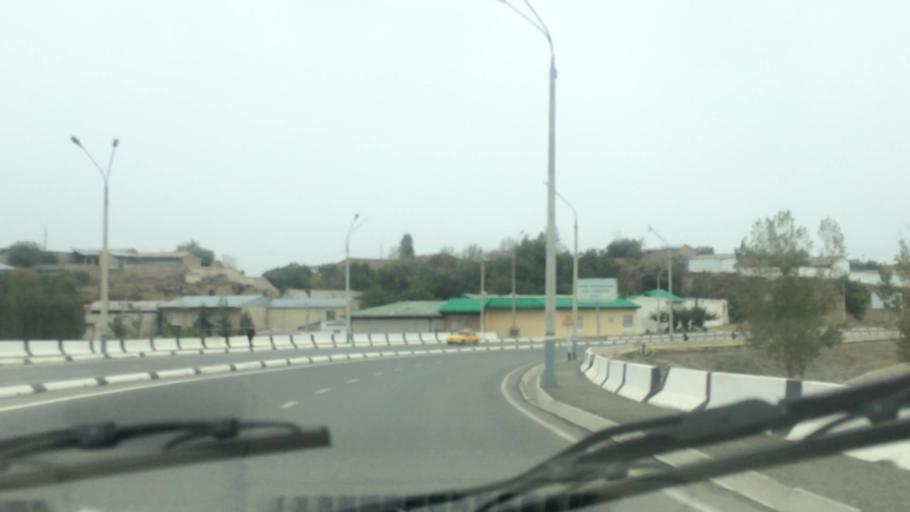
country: UZ
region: Samarqand
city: Samarqand
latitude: 39.6715
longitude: 67.0001
